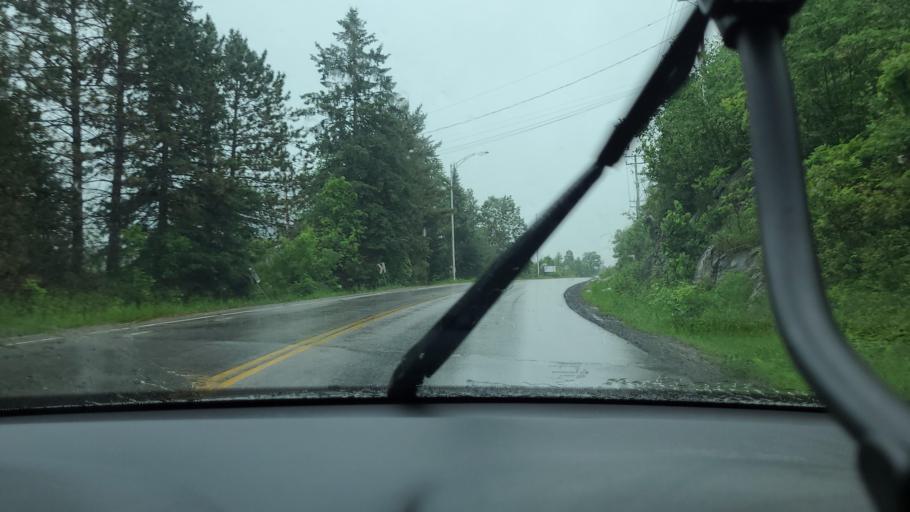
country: CA
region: Quebec
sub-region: Outaouais
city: Papineauville
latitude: 45.6693
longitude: -75.0172
